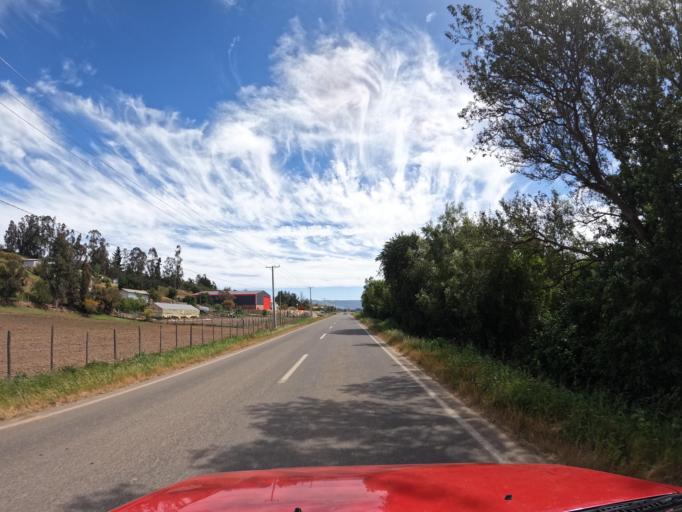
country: CL
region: Maule
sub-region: Provincia de Talca
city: Constitucion
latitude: -34.9969
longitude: -72.0218
